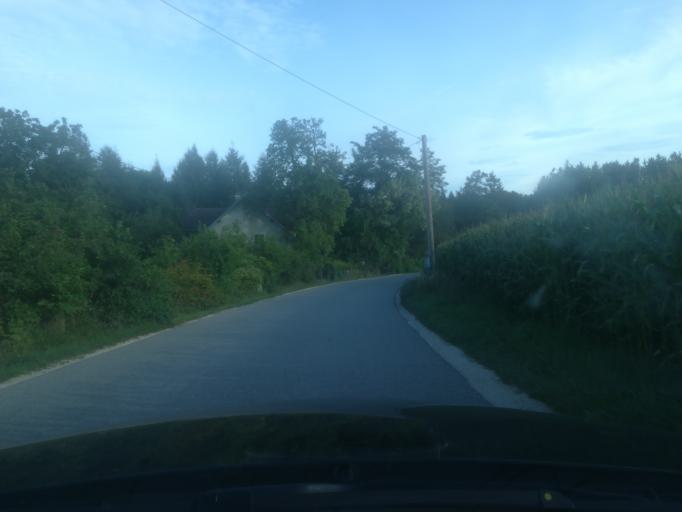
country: AT
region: Upper Austria
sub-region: Wels-Land
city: Marchtrenk
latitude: 48.1589
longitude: 14.1687
